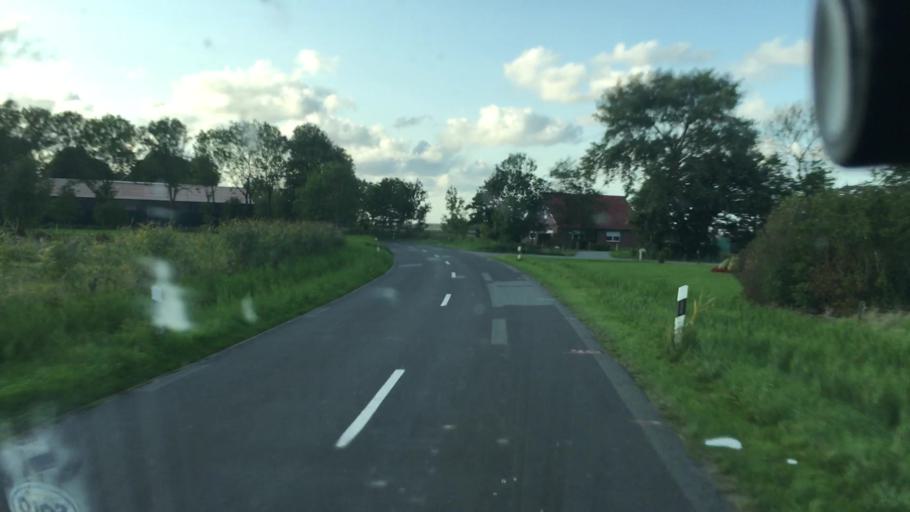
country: DE
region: Lower Saxony
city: Werdum
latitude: 53.6721
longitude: 7.7231
